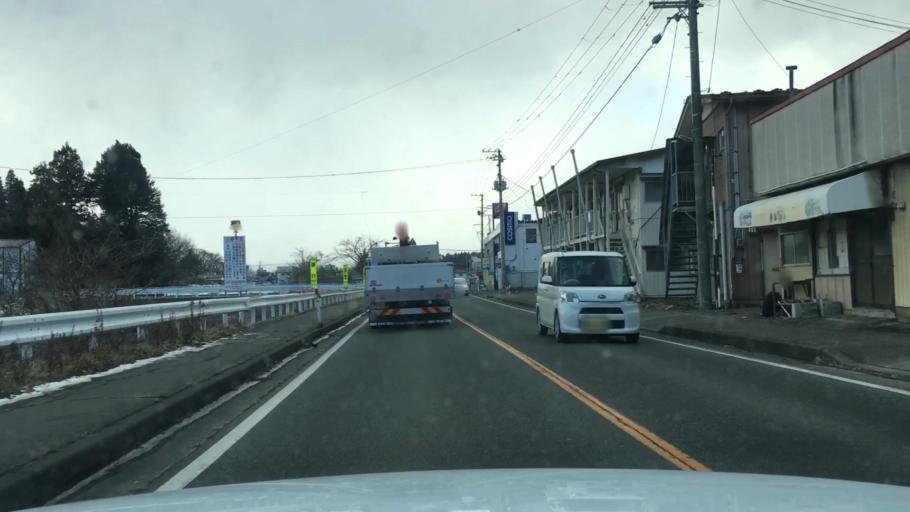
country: JP
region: Iwate
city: Morioka-shi
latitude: 39.6874
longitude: 141.1803
